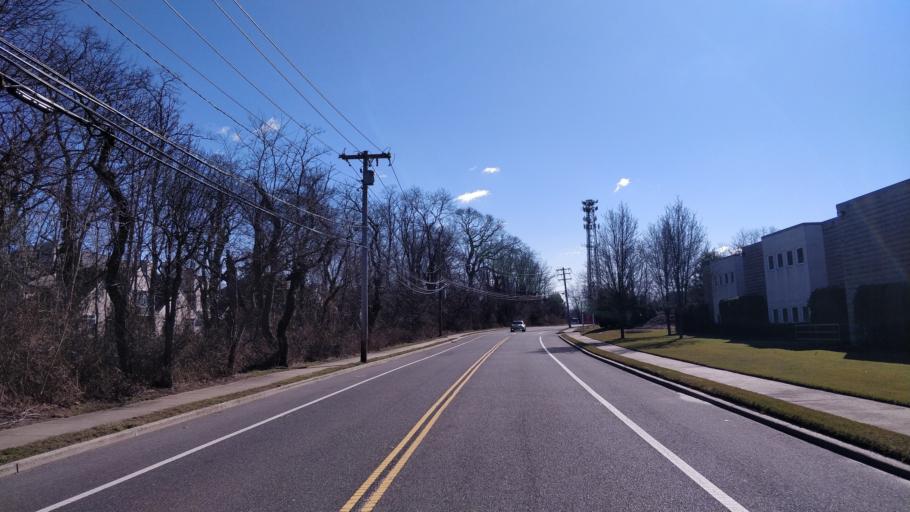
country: US
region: New York
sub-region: Suffolk County
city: Port Jefferson
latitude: 40.9352
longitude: -73.0818
